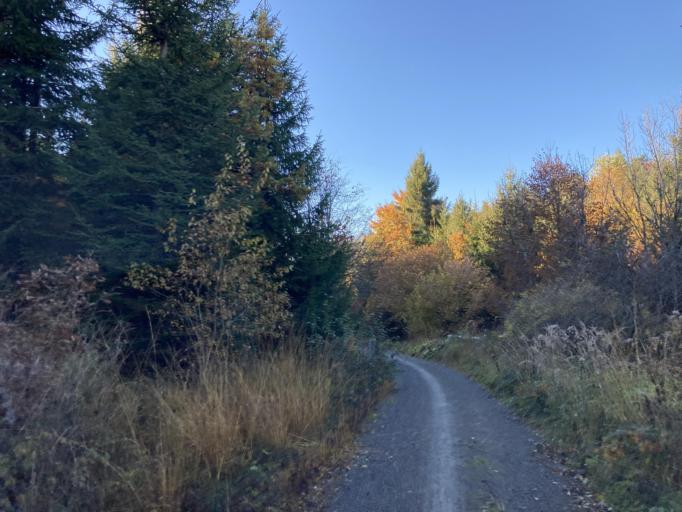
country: DE
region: Baden-Wuerttemberg
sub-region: Tuebingen Region
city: Bodelshausen
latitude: 48.4221
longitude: 8.9891
